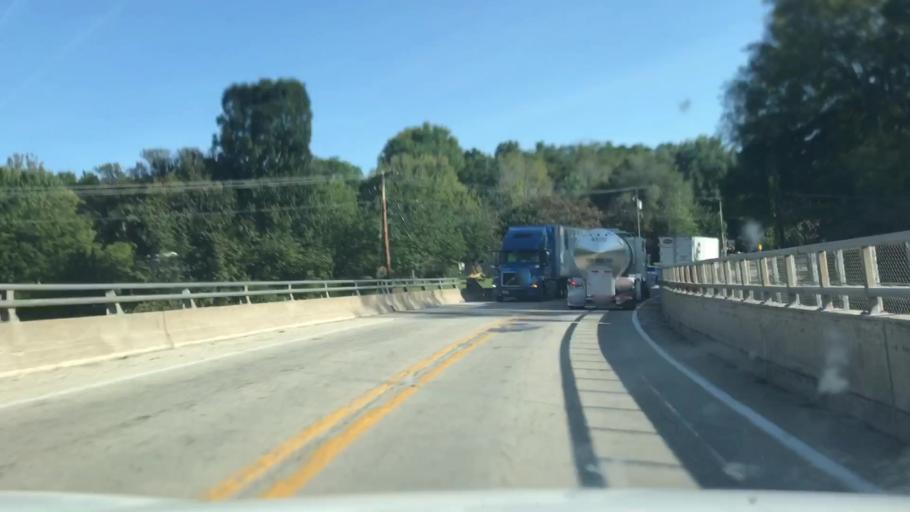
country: US
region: Illinois
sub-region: Adams County
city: Quincy
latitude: 39.8411
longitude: -91.3694
